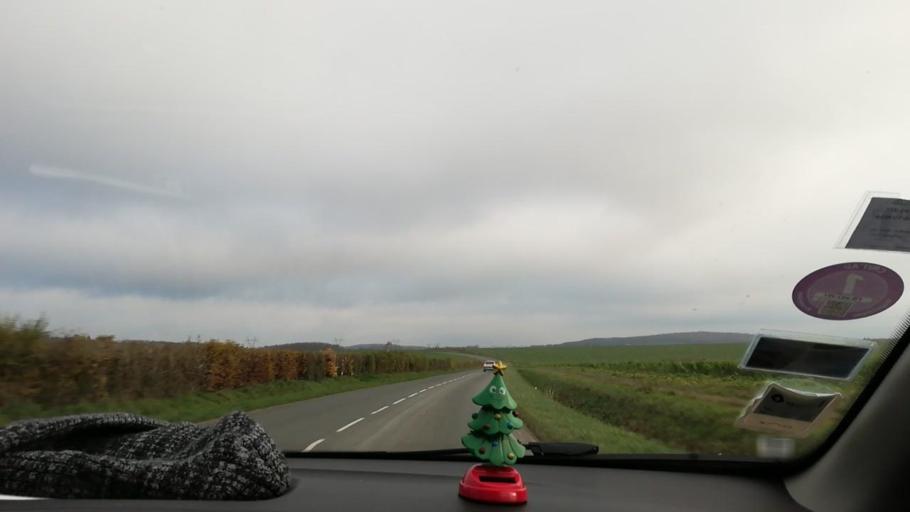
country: FR
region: Ile-de-France
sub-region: Departement de Seine-et-Marne
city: Monthyon
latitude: 48.9998
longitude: 2.8006
